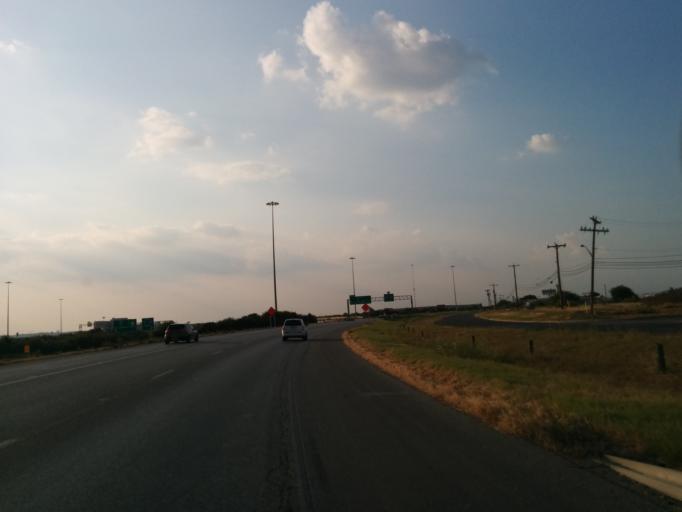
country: US
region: Texas
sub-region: Bexar County
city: Kirby
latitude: 29.4481
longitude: -98.4026
